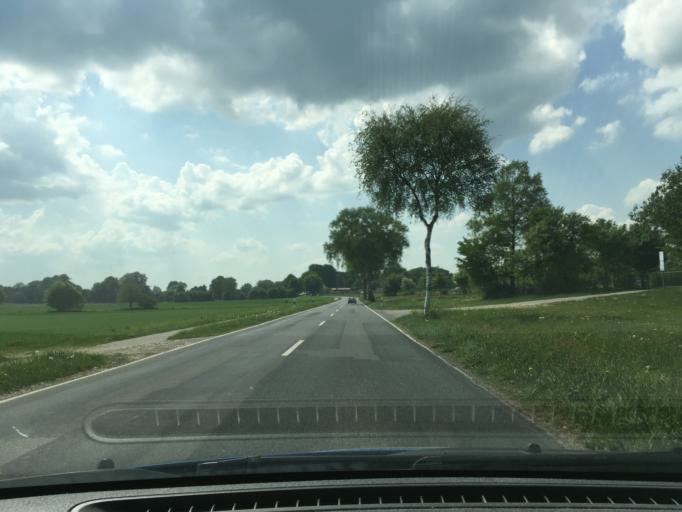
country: DE
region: Lower Saxony
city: Seevetal
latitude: 53.4278
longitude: 9.9005
